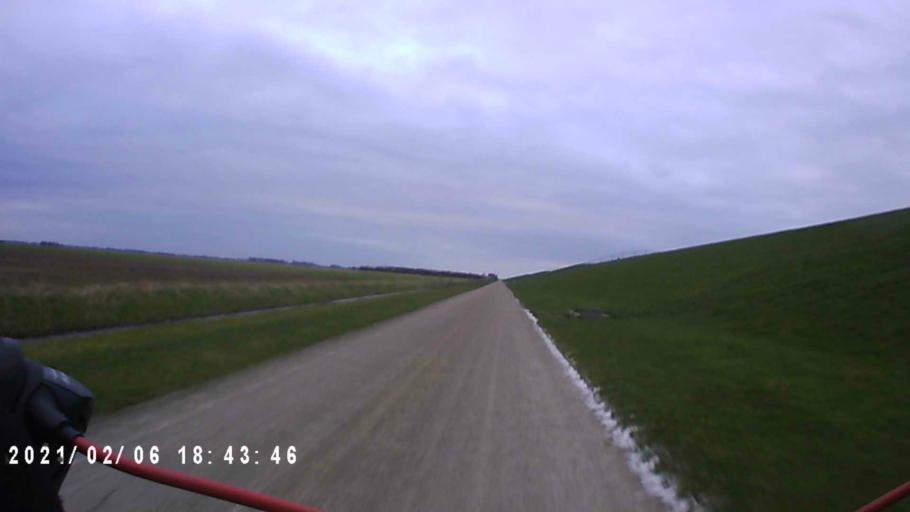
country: NL
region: Groningen
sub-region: Gemeente Winsum
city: Winsum
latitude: 53.4351
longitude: 6.5942
